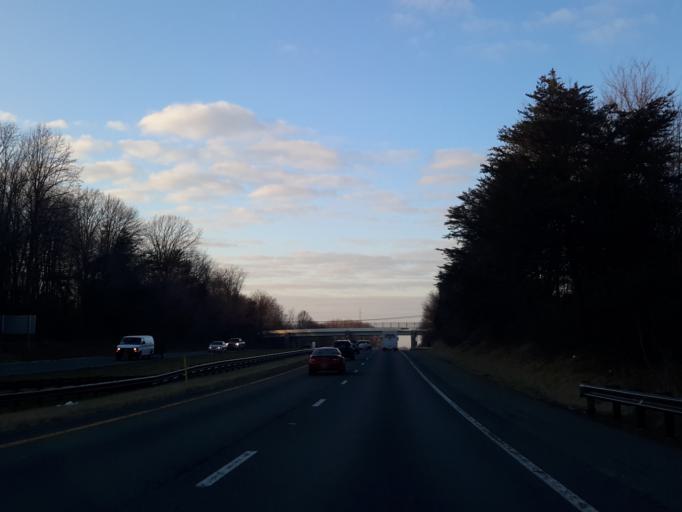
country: US
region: Maryland
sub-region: Montgomery County
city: Clarksburg
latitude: 39.2452
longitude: -77.2966
